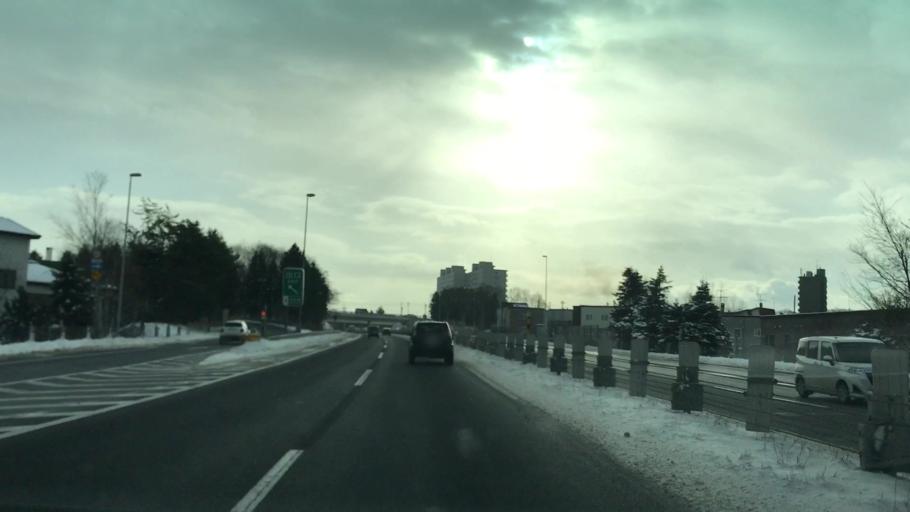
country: JP
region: Hokkaido
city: Kitahiroshima
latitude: 42.9793
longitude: 141.4758
